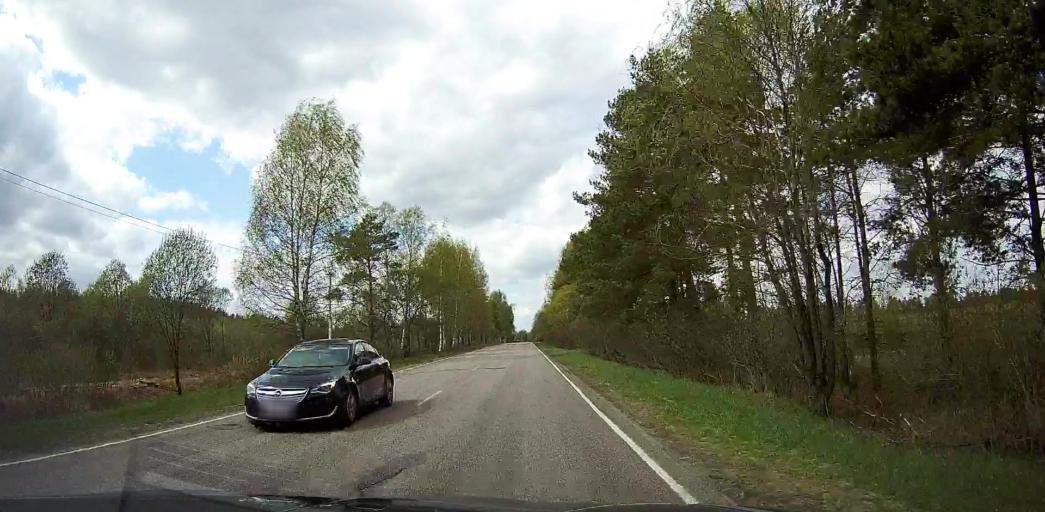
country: RU
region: Moskovskaya
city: Davydovo
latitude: 55.6600
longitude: 38.8108
